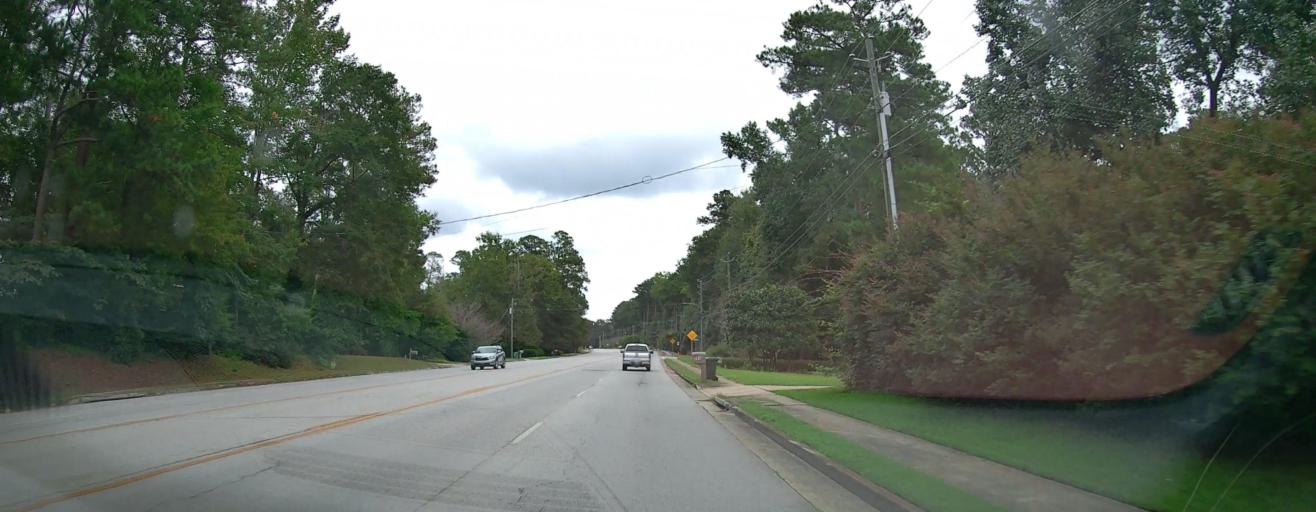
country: US
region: Georgia
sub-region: Bibb County
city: Macon
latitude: 32.8796
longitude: -83.7302
